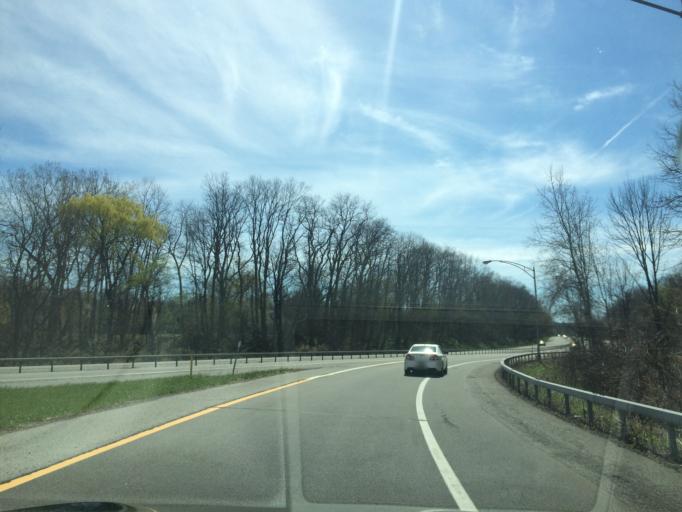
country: US
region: New York
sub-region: Monroe County
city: East Rochester
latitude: 43.0771
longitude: -77.4846
